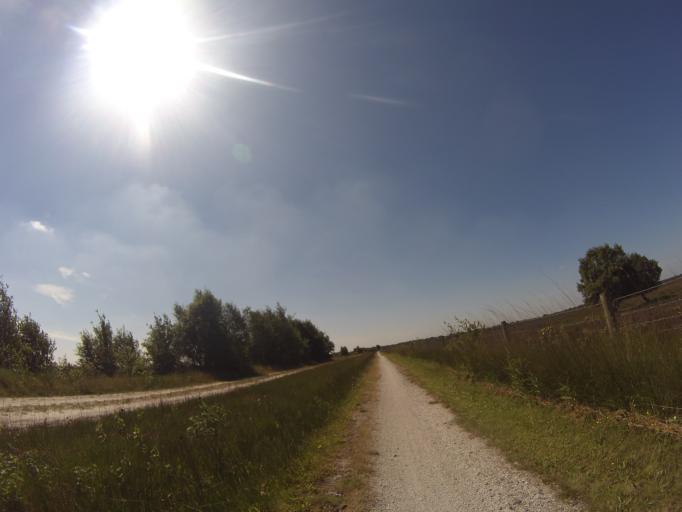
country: NL
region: Drenthe
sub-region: Gemeente Emmen
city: Klazienaveen
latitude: 52.6827
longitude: 7.0235
